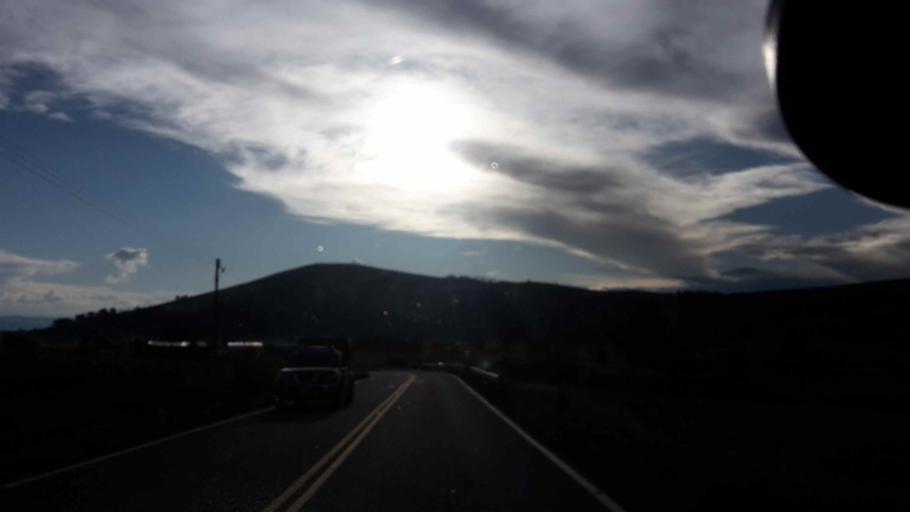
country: BO
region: Cochabamba
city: Arani
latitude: -17.5482
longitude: -65.6782
